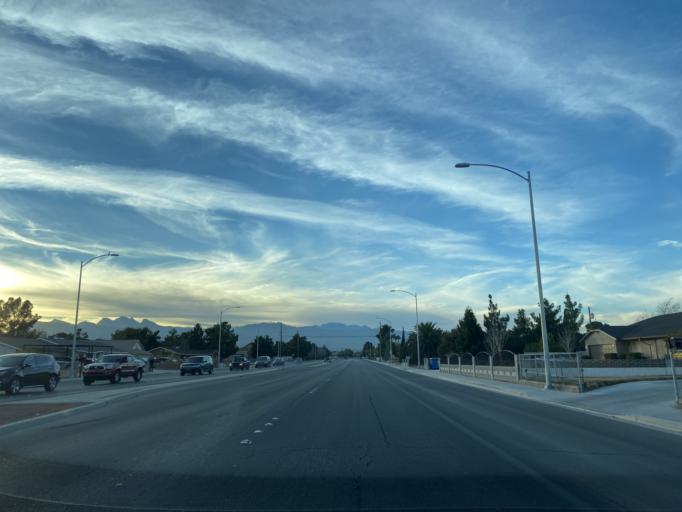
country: US
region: Nevada
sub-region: Clark County
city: Las Vegas
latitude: 36.2624
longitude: -115.2354
